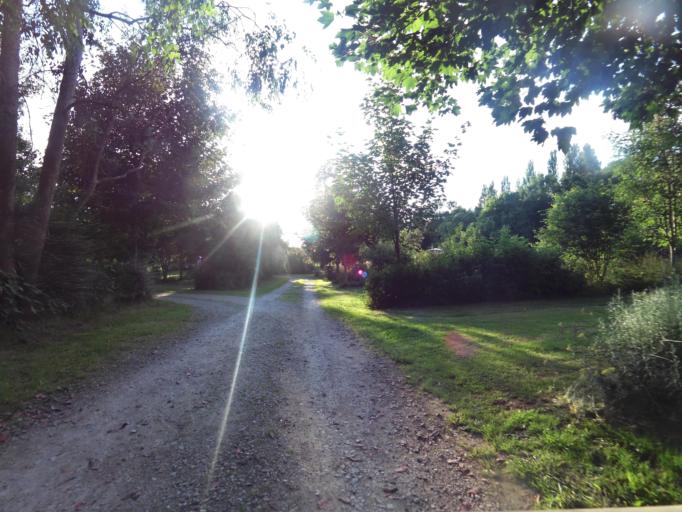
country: FR
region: Brittany
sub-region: Departement du Morbihan
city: Plougoumelen
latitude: 47.6442
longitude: -2.8998
